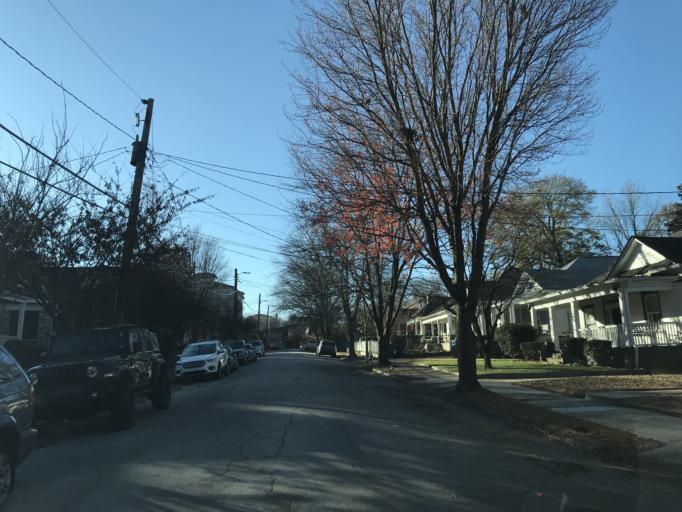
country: US
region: Georgia
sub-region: Fulton County
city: Atlanta
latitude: 33.7626
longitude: -84.3691
